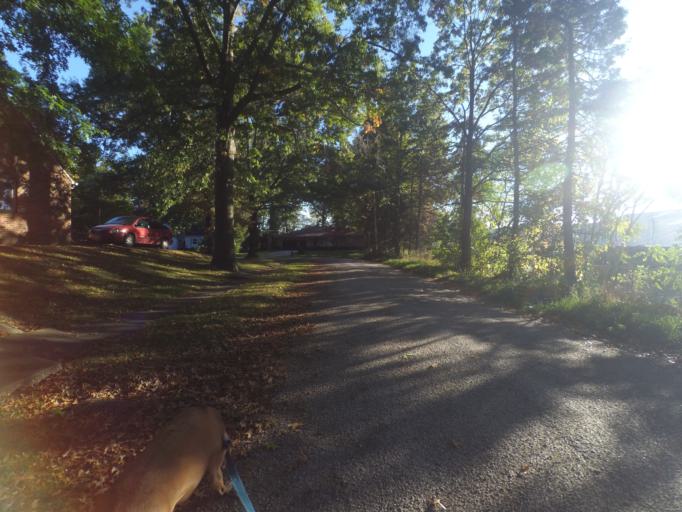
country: US
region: Ohio
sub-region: Portage County
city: Kent
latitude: 41.1527
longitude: -81.3716
